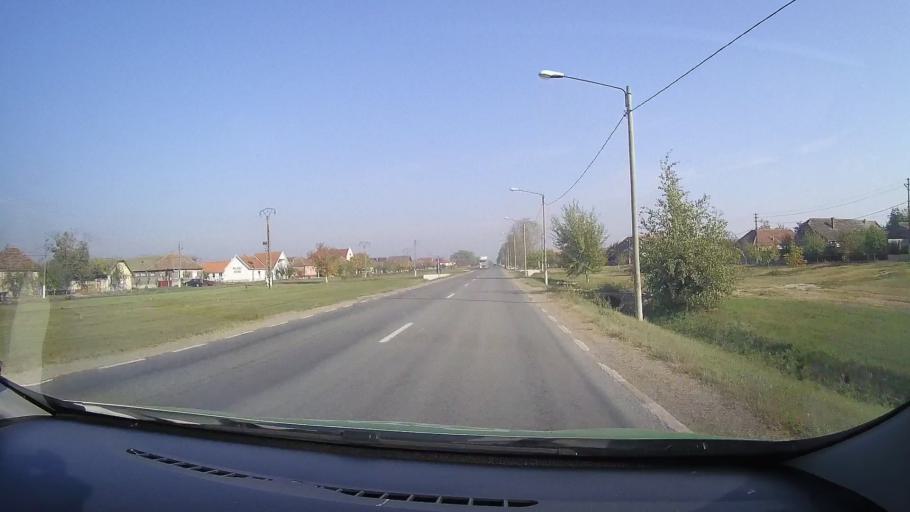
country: RO
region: Arad
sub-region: Comuna Pilu
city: Pilu
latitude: 46.5719
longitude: 21.3421
